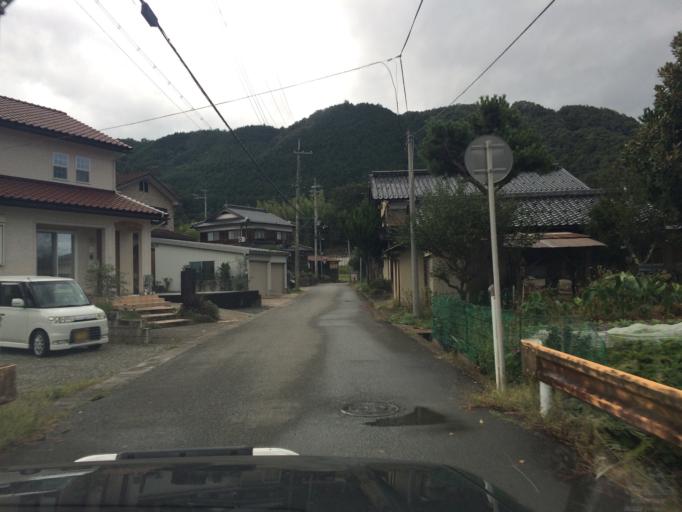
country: JP
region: Hyogo
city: Toyooka
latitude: 35.4560
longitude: 134.7703
